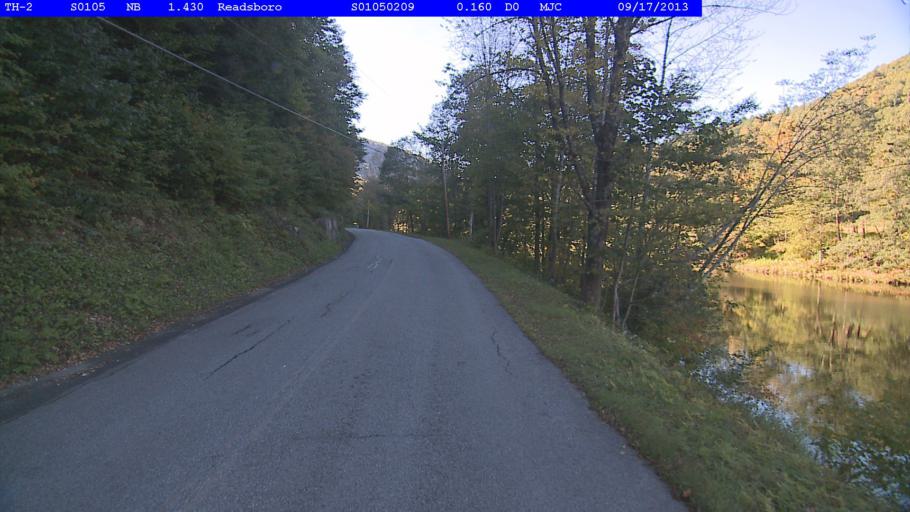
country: US
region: Massachusetts
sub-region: Franklin County
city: Charlemont
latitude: 42.7572
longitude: -72.9320
